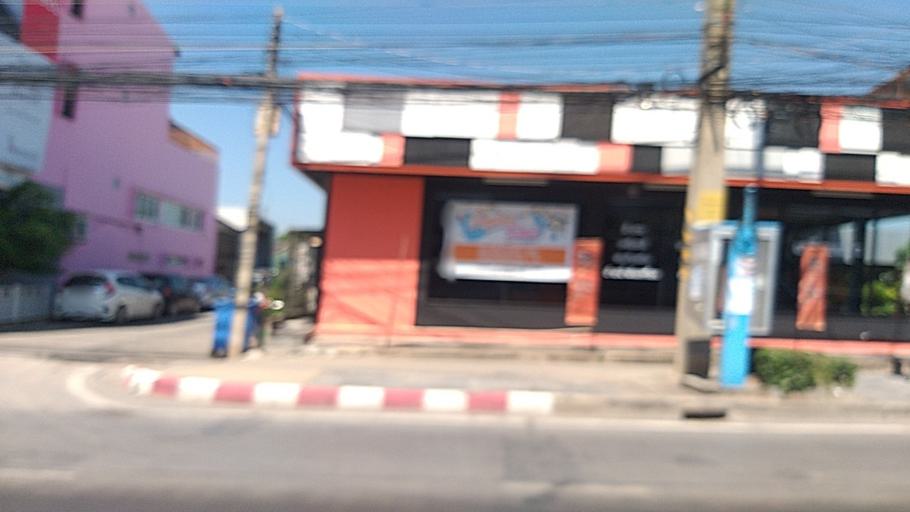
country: TH
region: Nakhon Ratchasima
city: Nakhon Ratchasima
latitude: 14.9796
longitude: 102.0832
